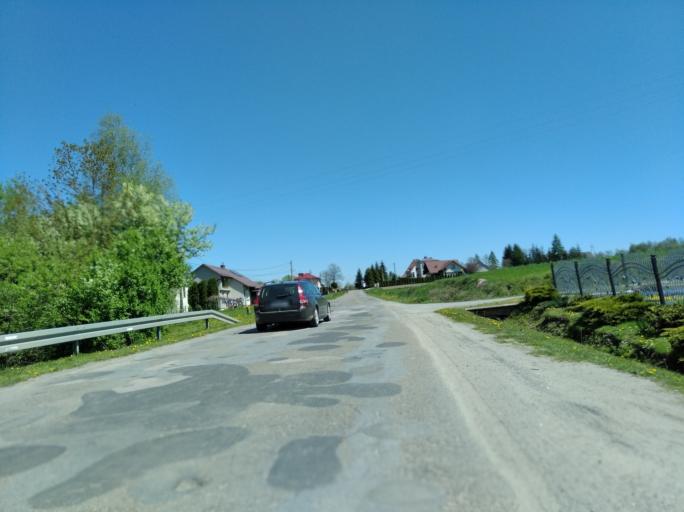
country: PL
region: Subcarpathian Voivodeship
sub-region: Powiat debicki
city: Brzostek
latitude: 49.9166
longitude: 21.4344
